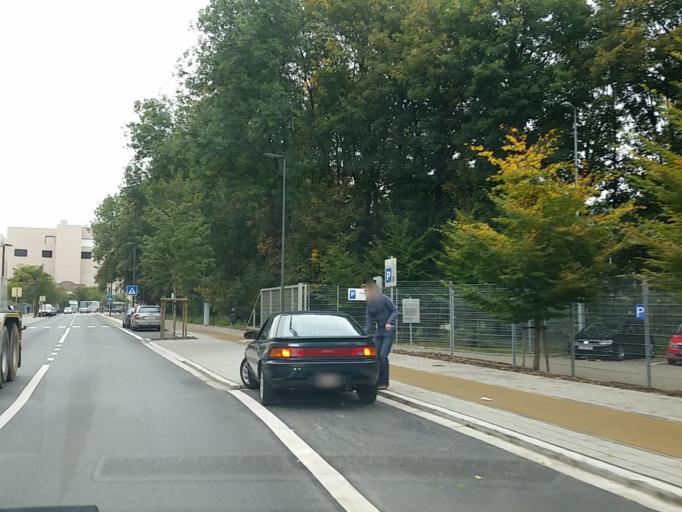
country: BE
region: Flanders
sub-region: Provincie Vlaams-Brabant
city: Drogenbos
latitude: 50.8105
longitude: 4.3149
